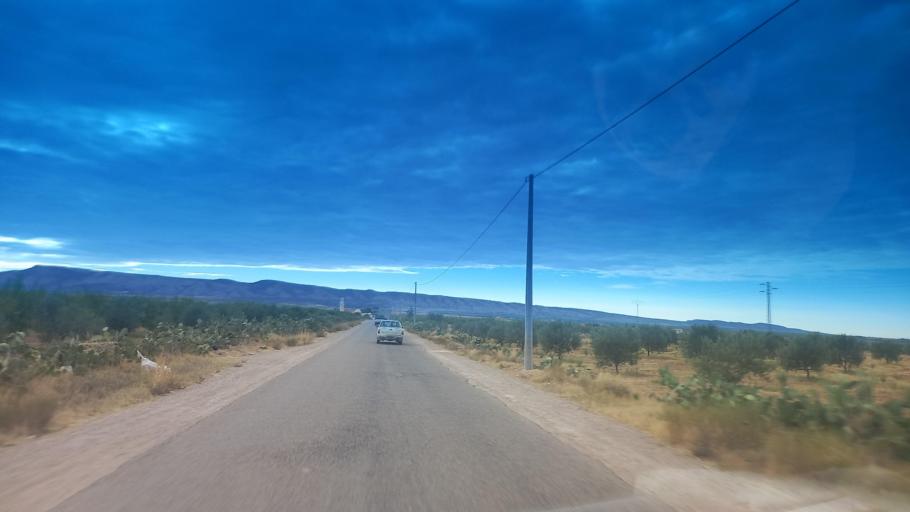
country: TN
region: Al Qasrayn
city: Sbiba
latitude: 35.3652
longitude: 9.0853
